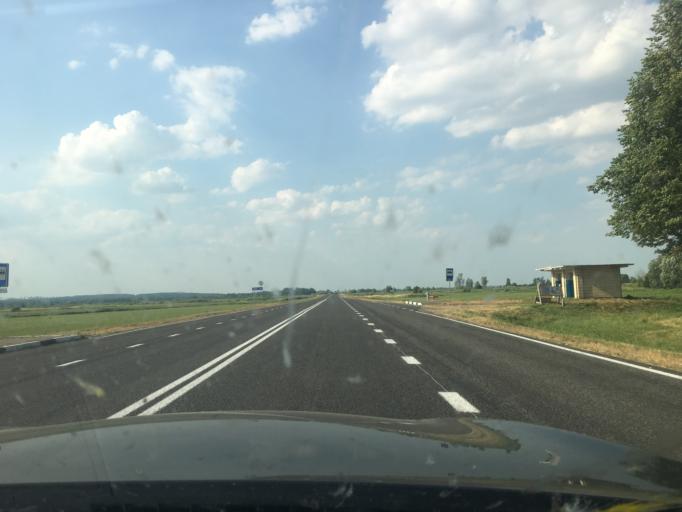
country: BY
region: Grodnenskaya
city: Indura
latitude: 53.3911
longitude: 23.9516
